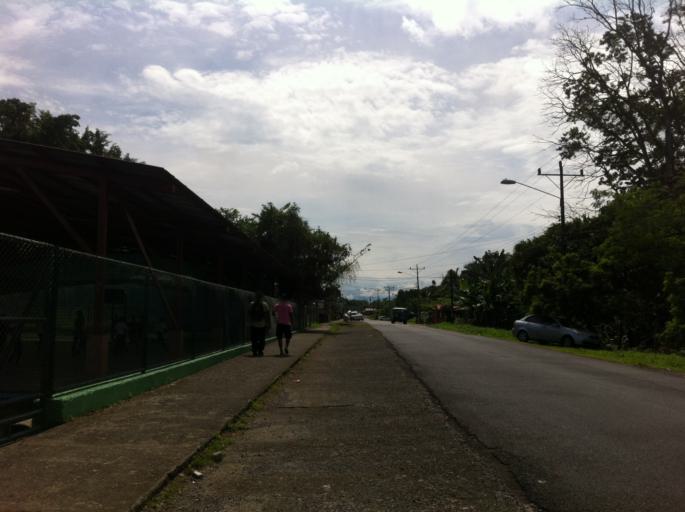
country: CR
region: Heredia
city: La Virgen
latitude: 10.3400
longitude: -83.9576
